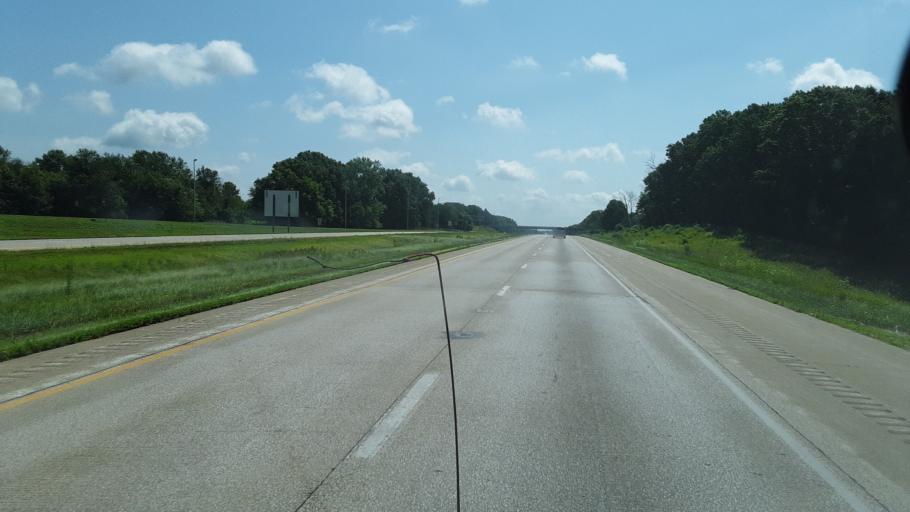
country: US
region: Illinois
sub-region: Clark County
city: Marshall
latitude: 39.4217
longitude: -87.6603
